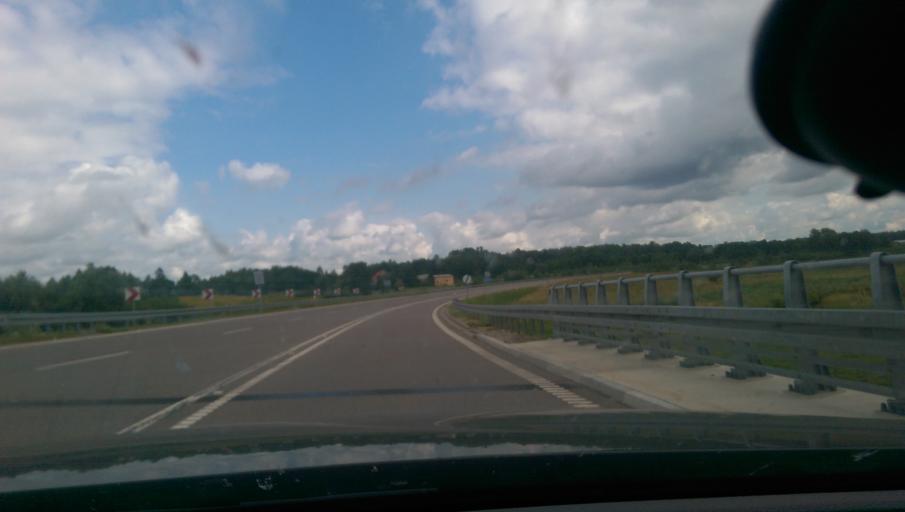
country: PL
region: Warmian-Masurian Voivodeship
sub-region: Powiat goldapski
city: Goldap
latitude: 54.3120
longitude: 22.2795
